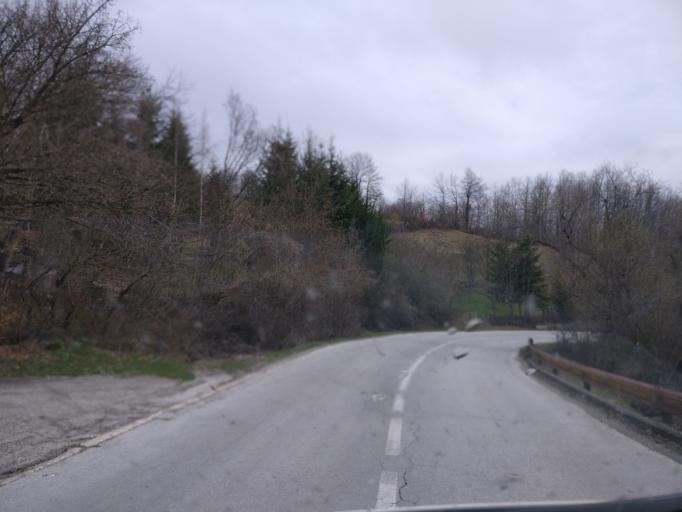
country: ME
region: Opstina Pluzine
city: Pluzine
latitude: 43.1229
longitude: 18.8147
